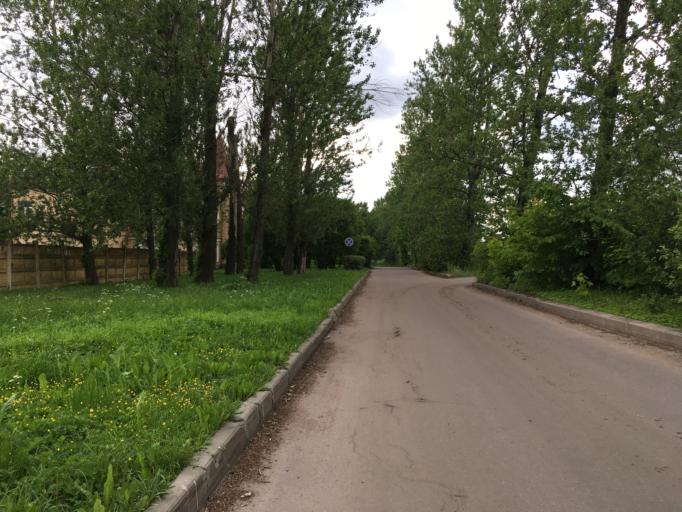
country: RU
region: St.-Petersburg
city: Centralniy
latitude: 59.9051
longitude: 30.3731
